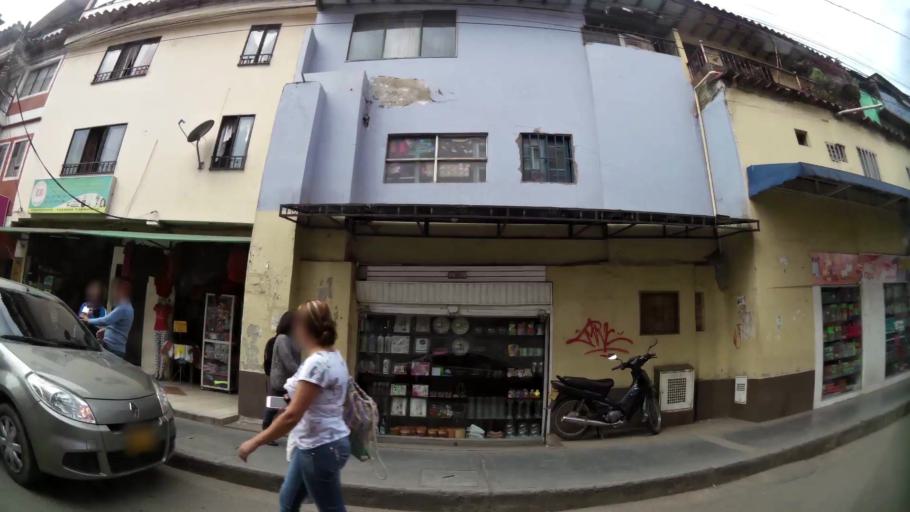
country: CO
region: Antioquia
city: Rionegro
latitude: 6.1553
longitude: -75.3722
